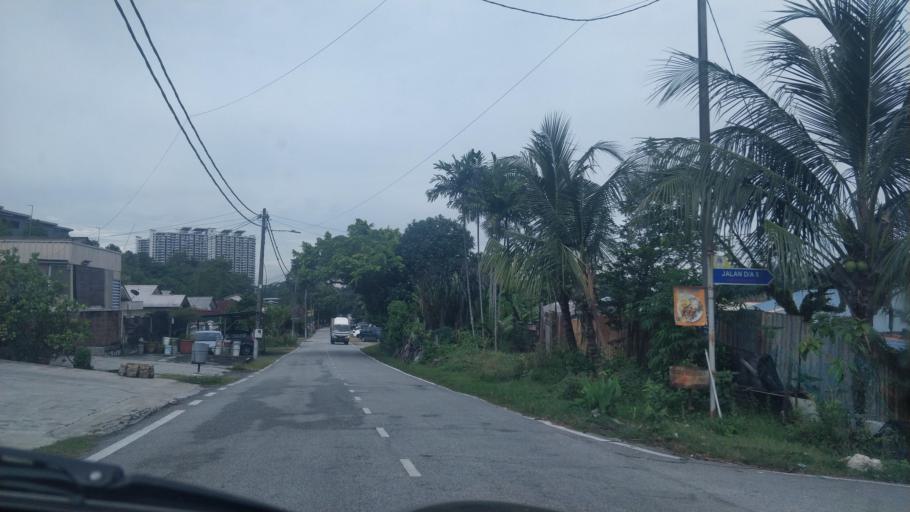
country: MY
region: Selangor
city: Kuang
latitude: 3.2049
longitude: 101.5975
